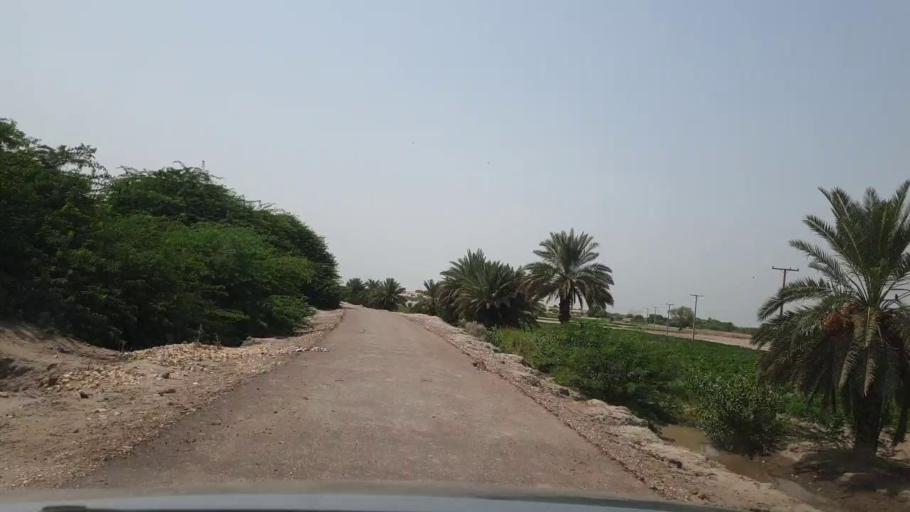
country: PK
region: Sindh
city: Pano Aqil
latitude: 27.6105
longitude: 69.1458
